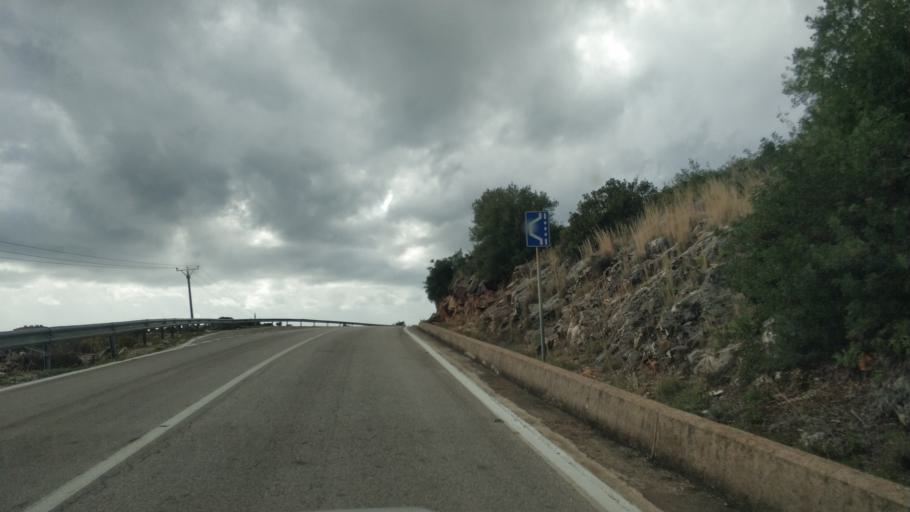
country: AL
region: Vlore
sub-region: Rrethi i Vlores
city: Vranisht
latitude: 40.1448
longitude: 19.6575
